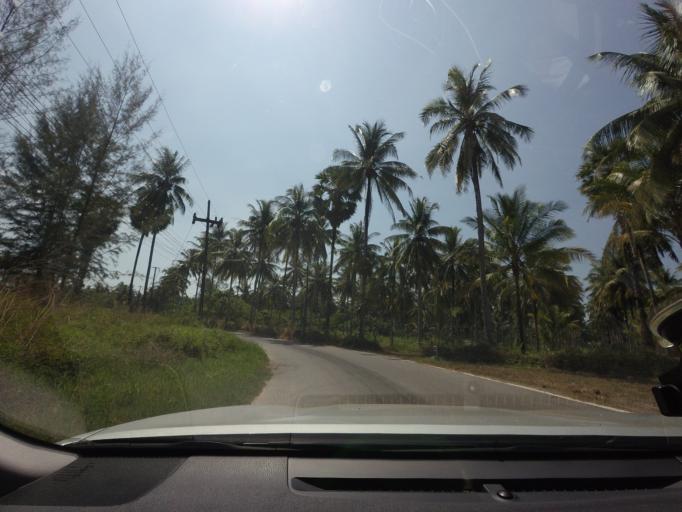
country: TH
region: Phangnga
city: Ban Khao Lak
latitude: 8.6973
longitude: 98.2467
